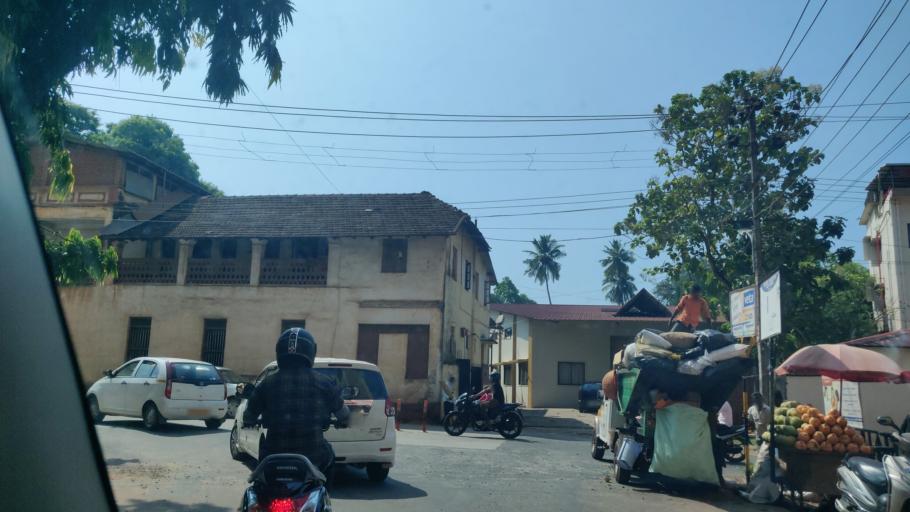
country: IN
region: Karnataka
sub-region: Dakshina Kannada
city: Mangalore
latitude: 12.8691
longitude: 74.8404
